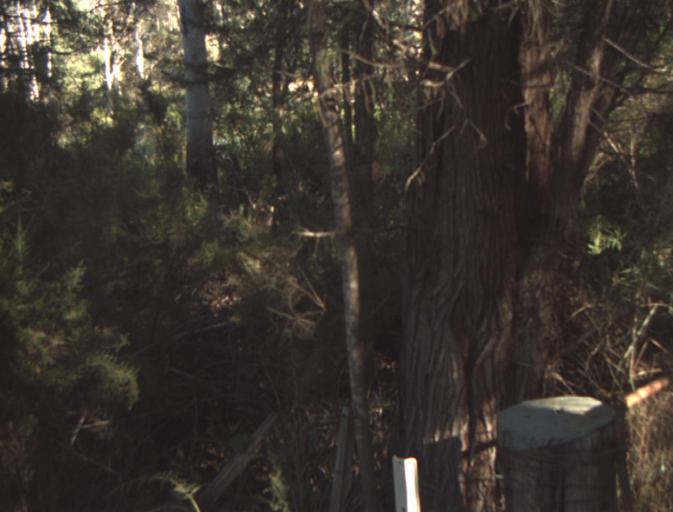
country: AU
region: Tasmania
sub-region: Launceston
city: Mayfield
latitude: -41.2908
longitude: 147.1812
